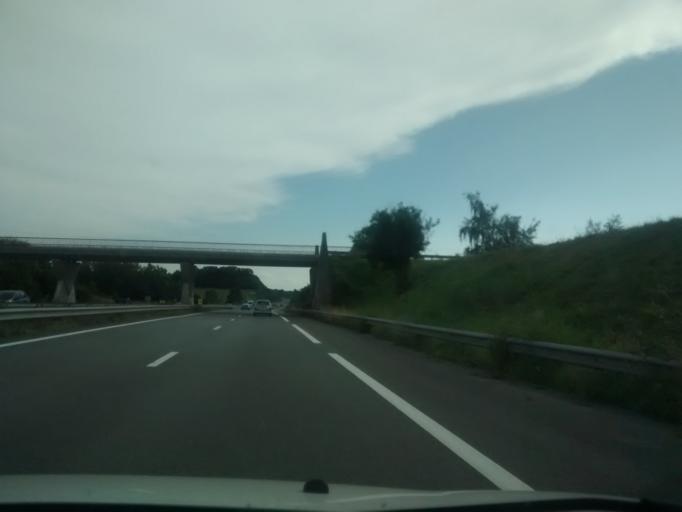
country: FR
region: Brittany
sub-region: Departement d'Ille-et-Vilaine
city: Saint-Pierre-de-Plesguen
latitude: 48.4602
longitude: -1.9168
